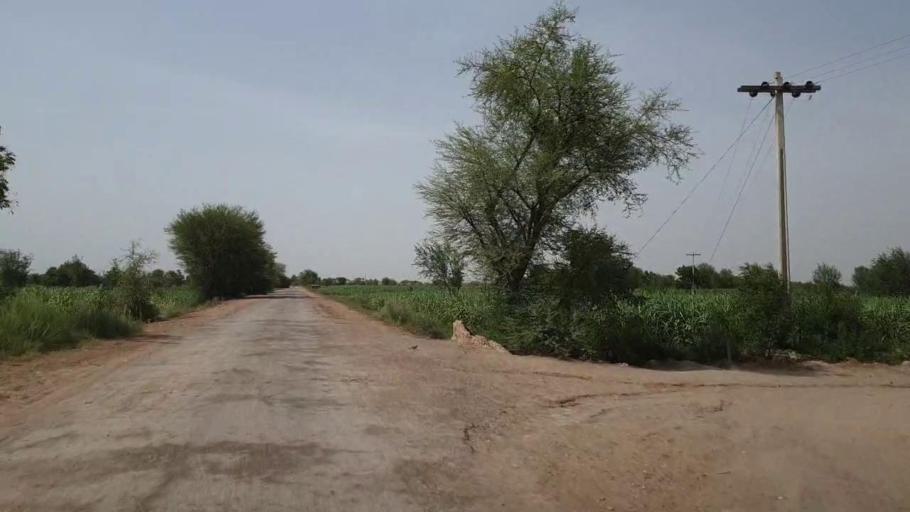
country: PK
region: Sindh
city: Daur
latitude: 26.5337
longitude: 68.4076
